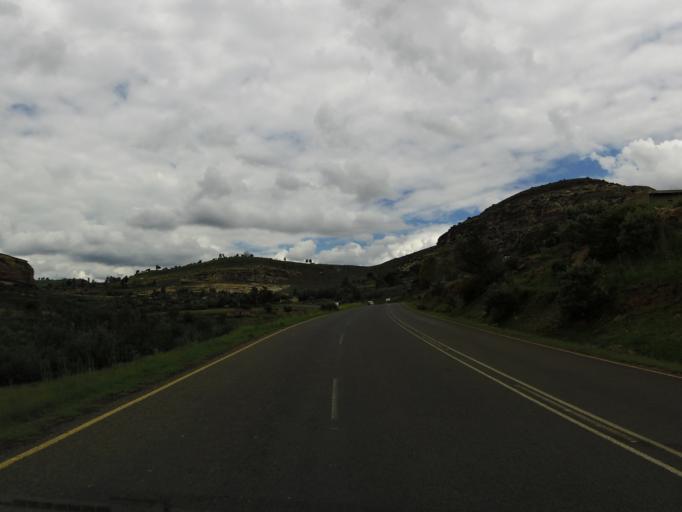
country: LS
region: Leribe
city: Leribe
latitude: -28.9842
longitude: 28.1828
